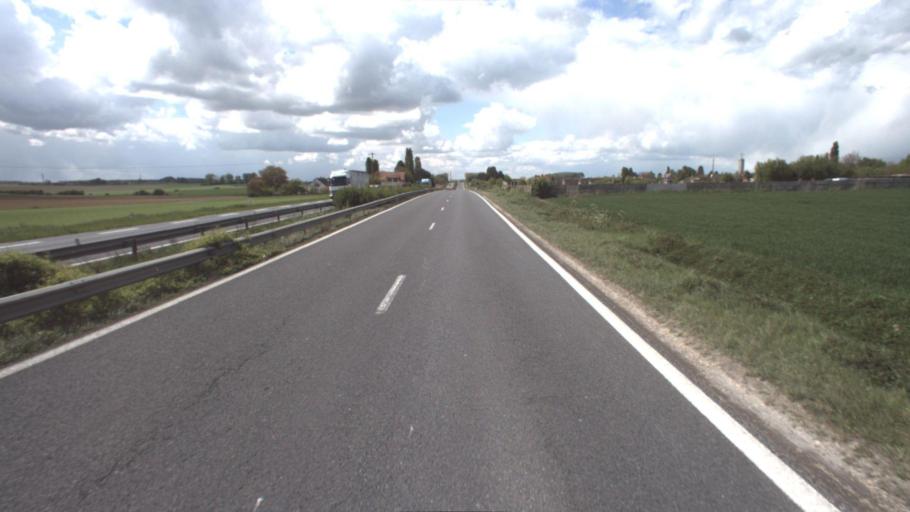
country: FR
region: Ile-de-France
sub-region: Departement de Seine-et-Marne
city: Jouy-le-Chatel
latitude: 48.6844
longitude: 3.0861
